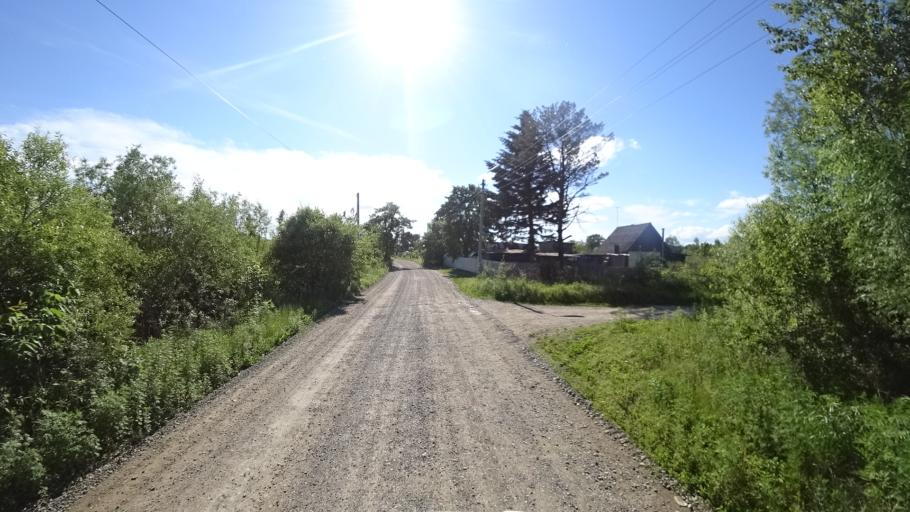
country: RU
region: Khabarovsk Krai
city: Khor
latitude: 47.8868
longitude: 135.0126
